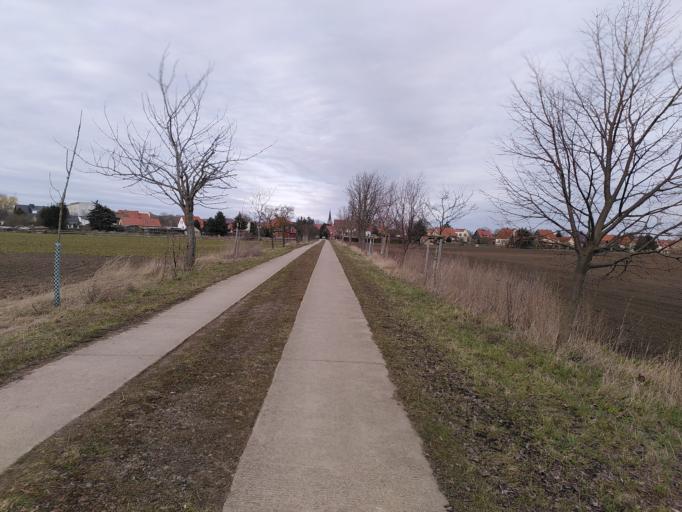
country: DE
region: Saxony-Anhalt
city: Gatersleben
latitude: 51.8171
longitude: 11.2800
